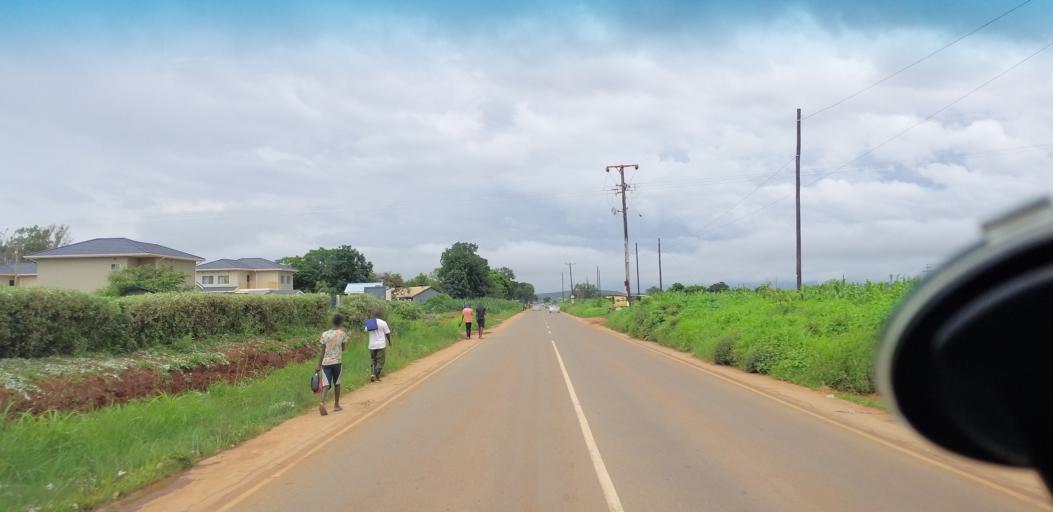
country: ZM
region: Lusaka
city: Lusaka
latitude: -15.5170
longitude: 28.2978
